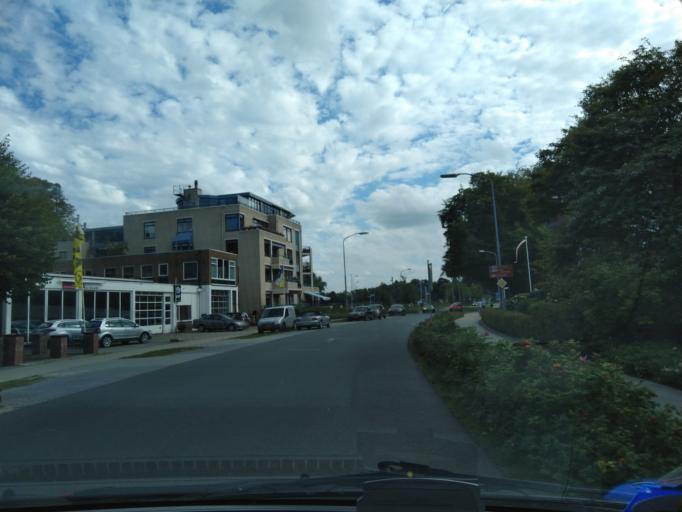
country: NL
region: Groningen
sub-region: Gemeente Haren
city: Haren
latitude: 53.1586
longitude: 6.5630
